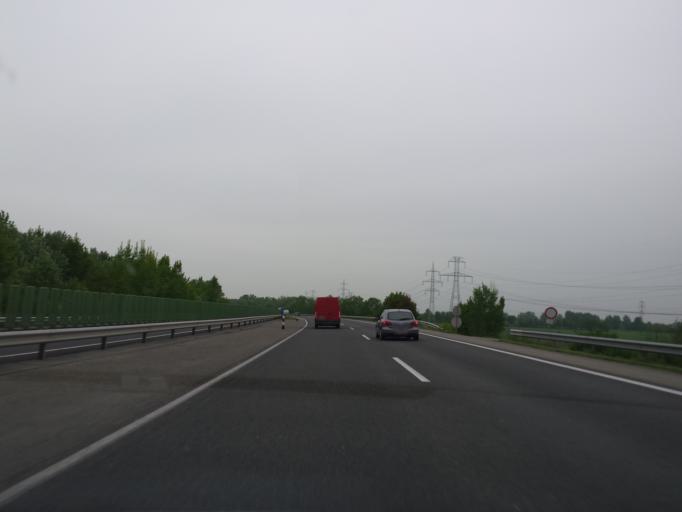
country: HU
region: Gyor-Moson-Sopron
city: Abda
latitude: 47.6861
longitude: 17.5388
